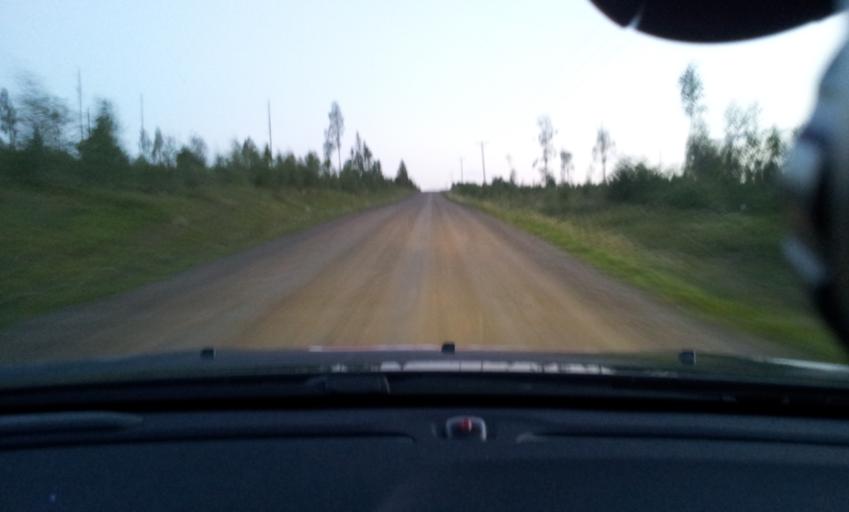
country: SE
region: Vaesternorrland
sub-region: Ange Kommun
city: Ange
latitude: 62.7604
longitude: 15.6856
